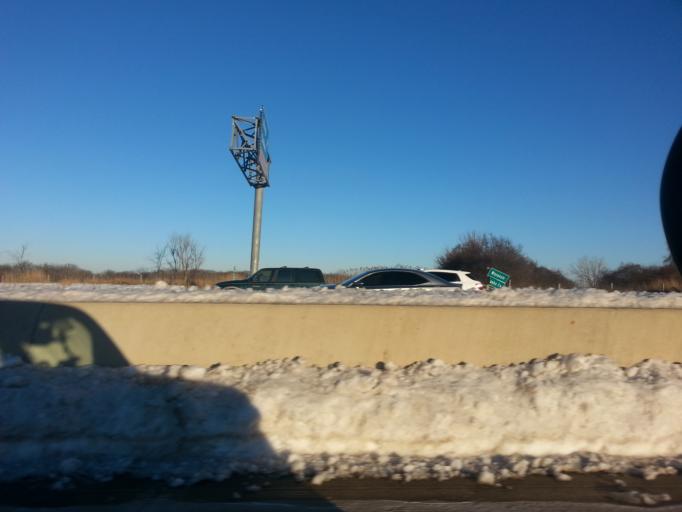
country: US
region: Wisconsin
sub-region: Kenosha County
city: Pleasant Prairie
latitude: 42.4946
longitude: -87.9500
